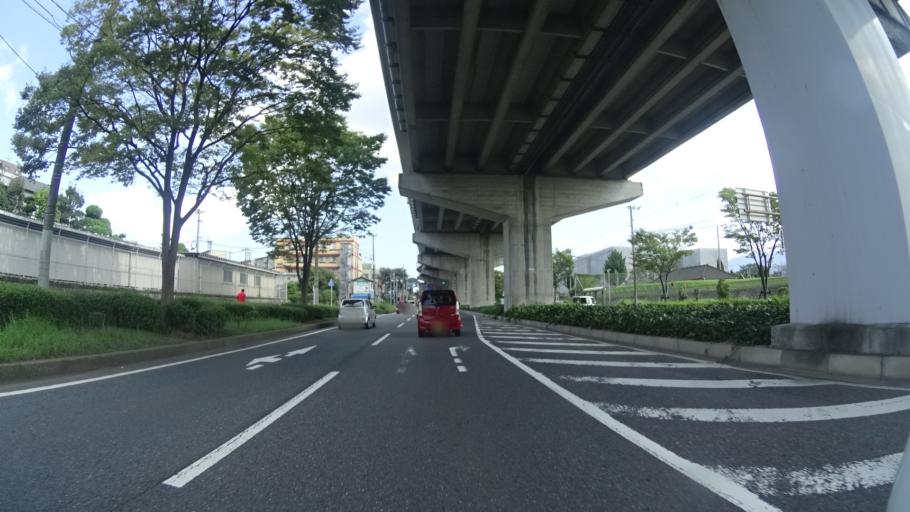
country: JP
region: Fukuoka
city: Kitakyushu
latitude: 33.8448
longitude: 130.8840
